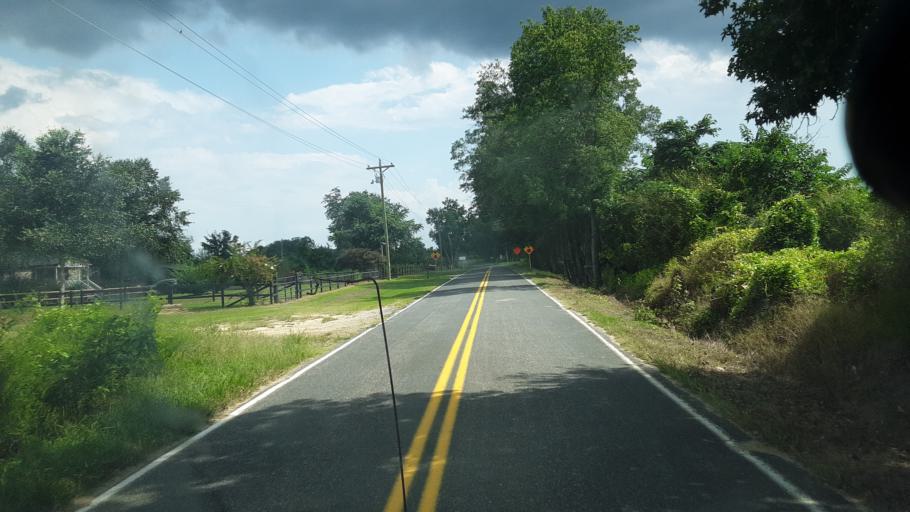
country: US
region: South Carolina
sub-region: Lee County
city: Bishopville
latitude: 34.1426
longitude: -80.1159
